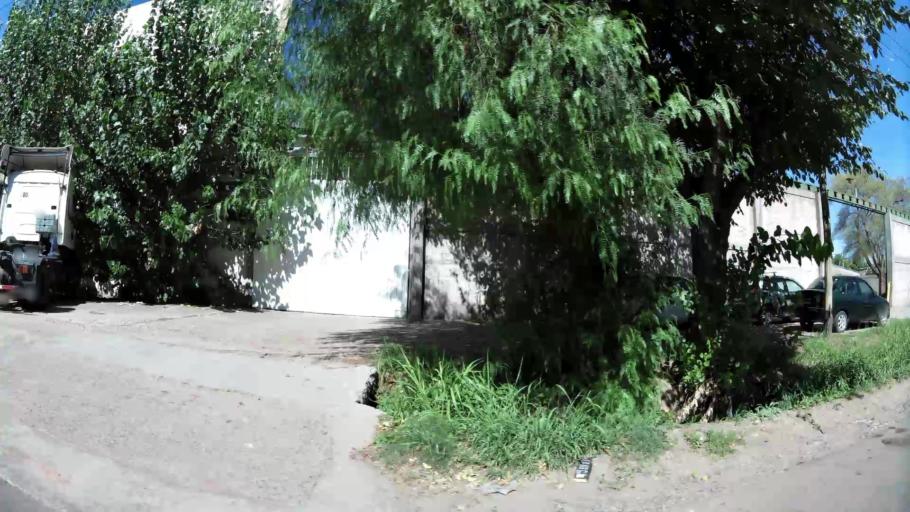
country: AR
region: Mendoza
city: Villa Nueva
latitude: -32.8896
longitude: -68.7829
